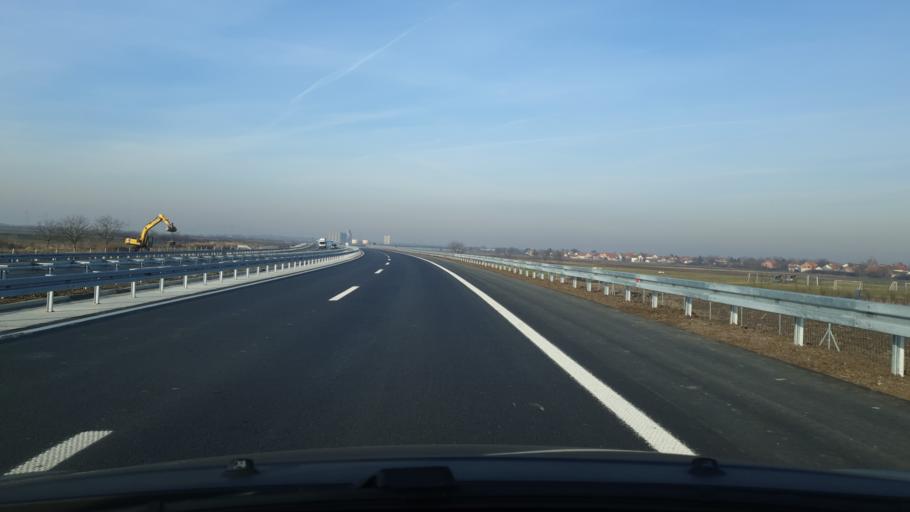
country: RS
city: Boljevci
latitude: 44.7513
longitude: 20.2502
